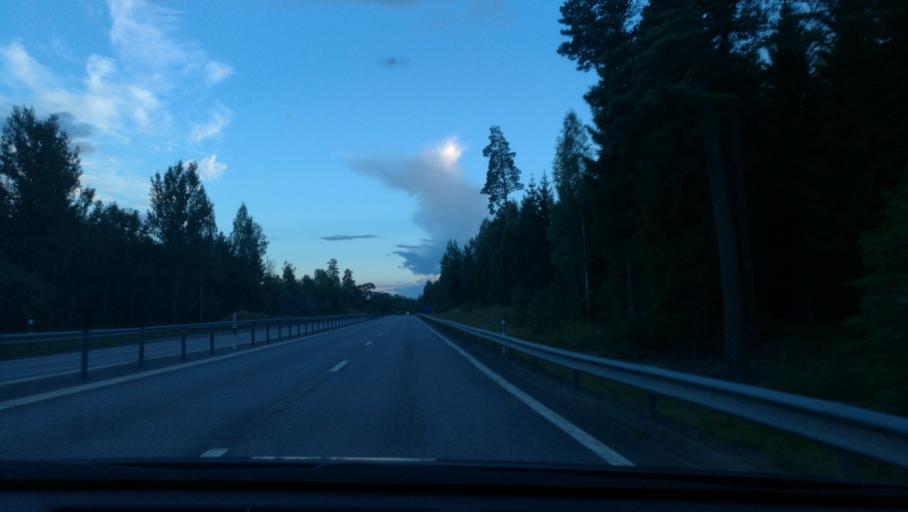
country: SE
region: Soedermanland
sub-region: Katrineholms Kommun
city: Katrineholm
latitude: 58.8503
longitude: 16.2053
